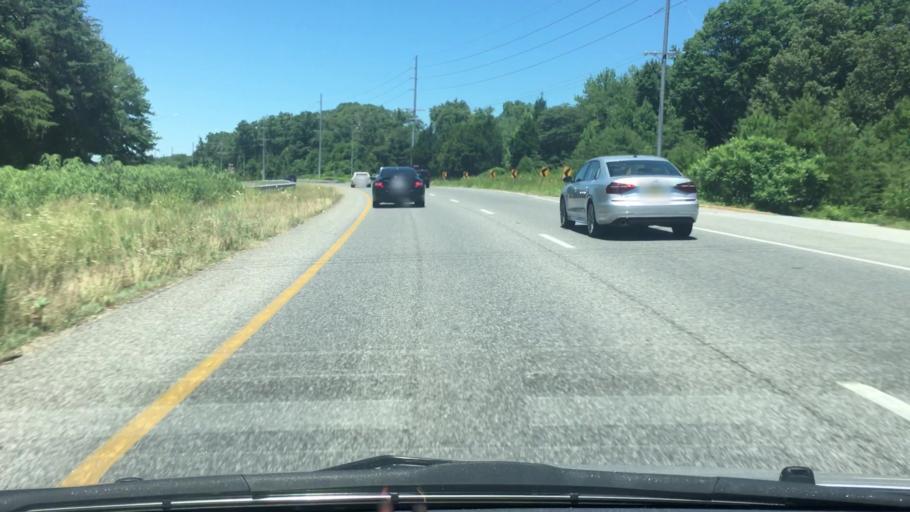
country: US
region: Maryland
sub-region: Charles County
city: Hughesville
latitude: 38.5155
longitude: -76.7745
